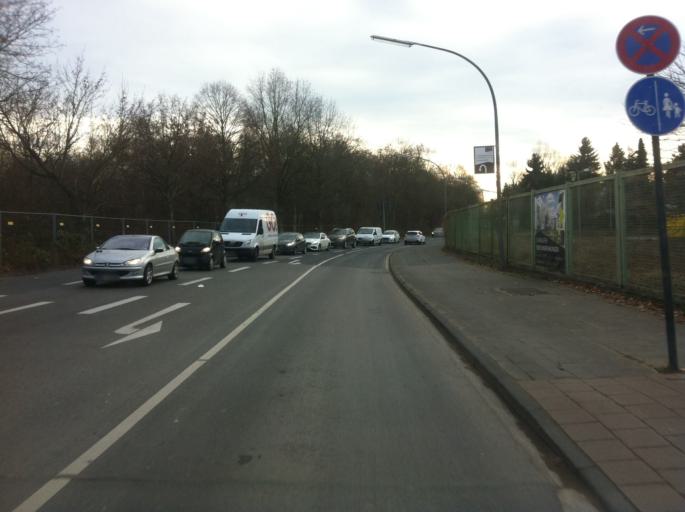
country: DE
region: North Rhine-Westphalia
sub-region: Regierungsbezirk Koln
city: Bilderstoeckchen
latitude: 50.9823
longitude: 6.9011
